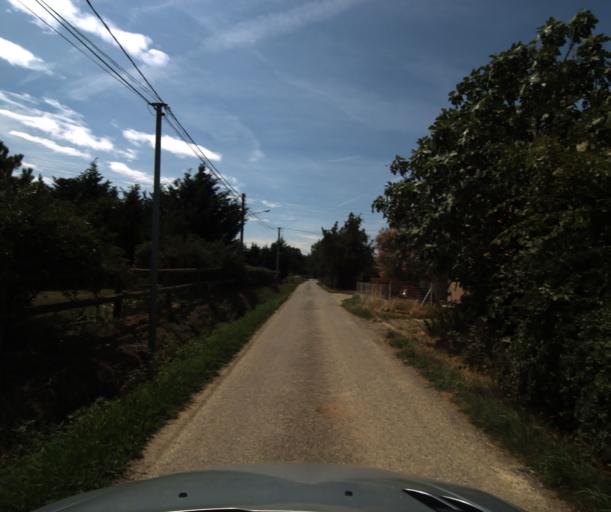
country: FR
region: Midi-Pyrenees
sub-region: Departement de la Haute-Garonne
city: Labastidette
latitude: 43.4467
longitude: 1.2376
